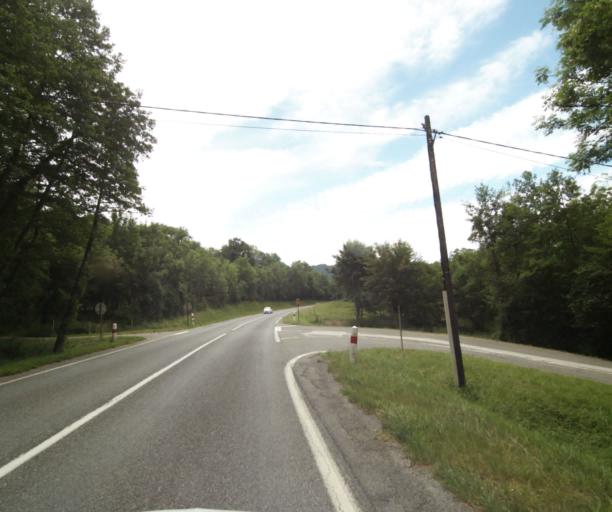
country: FR
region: Rhone-Alpes
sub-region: Departement de la Haute-Savoie
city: Allinges
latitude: 46.3441
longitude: 6.4645
